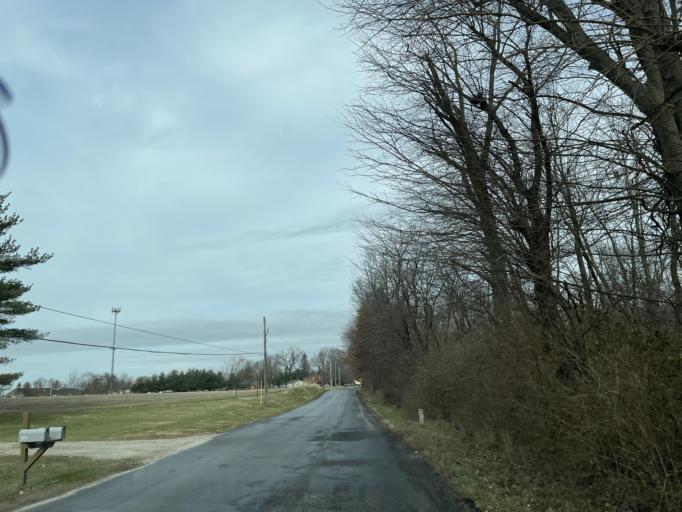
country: US
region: Illinois
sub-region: Sangamon County
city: Jerome
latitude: 39.7783
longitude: -89.7346
